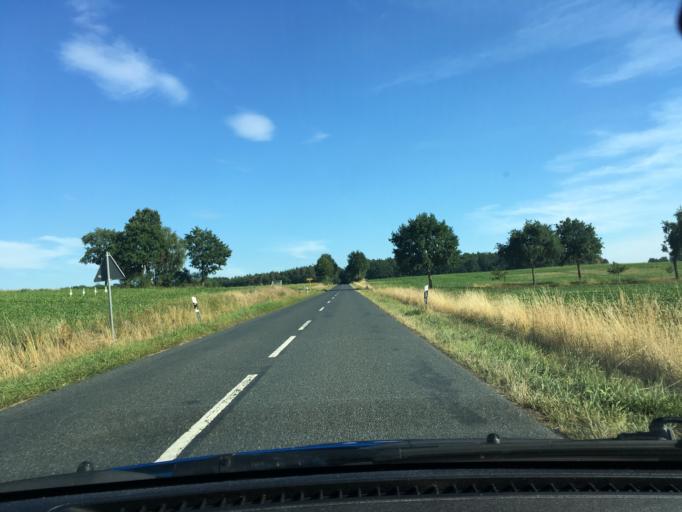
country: DE
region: Lower Saxony
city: Dahlenburg
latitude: 53.2126
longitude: 10.7034
